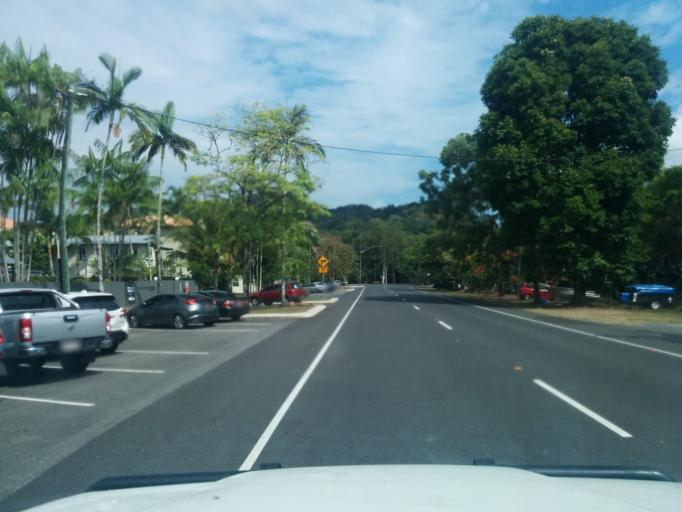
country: AU
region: Queensland
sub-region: Cairns
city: Cairns
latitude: -16.9027
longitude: 145.7554
